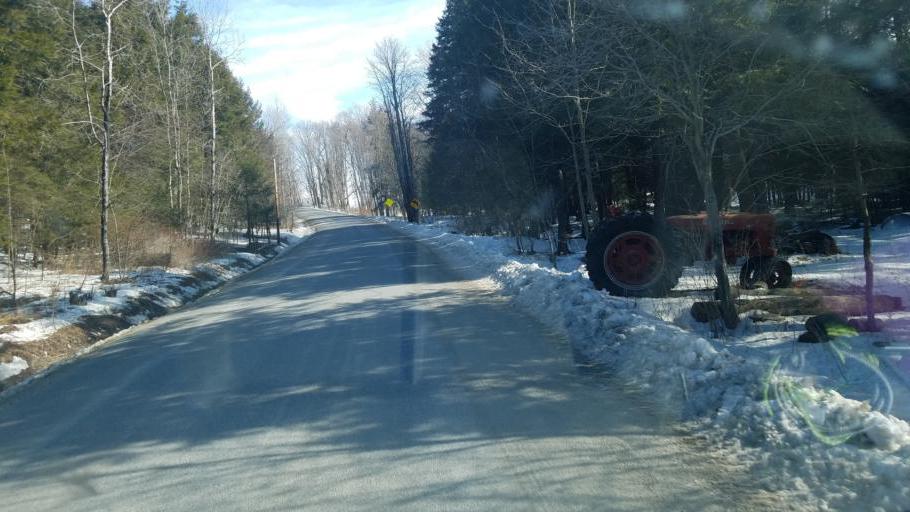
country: US
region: New York
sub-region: Allegany County
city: Andover
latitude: 42.0559
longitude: -77.7739
